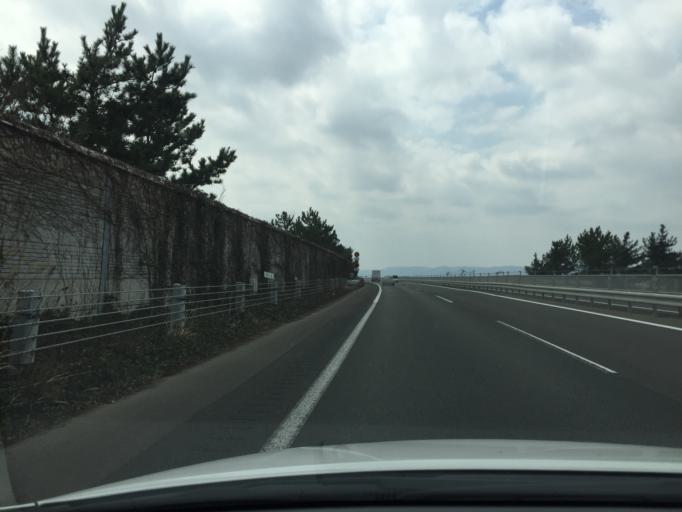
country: JP
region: Miyagi
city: Iwanuma
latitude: 38.1581
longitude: 140.8999
